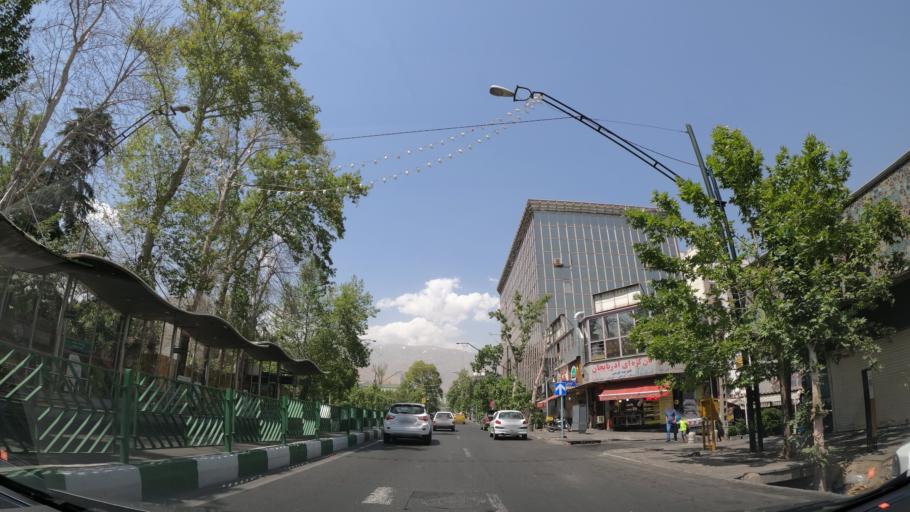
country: IR
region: Tehran
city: Tajrish
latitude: 35.7780
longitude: 51.4135
